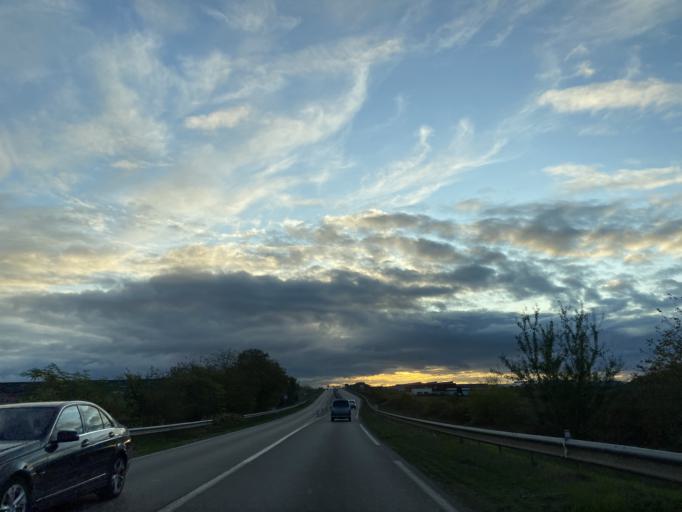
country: FR
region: Centre
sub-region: Departement du Cher
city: La Chapelle-Saint-Ursin
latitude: 47.0550
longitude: 2.3540
